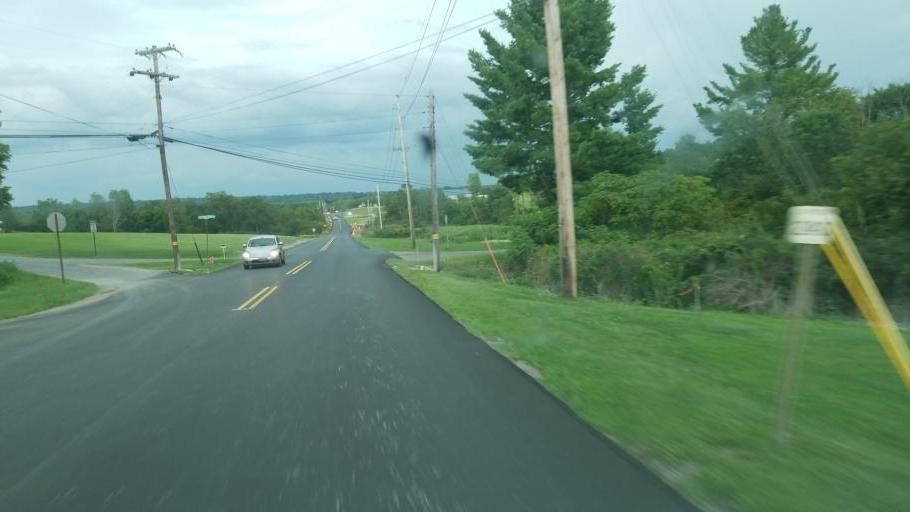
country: US
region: Pennsylvania
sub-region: Clarion County
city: Knox
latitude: 41.2446
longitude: -79.5388
